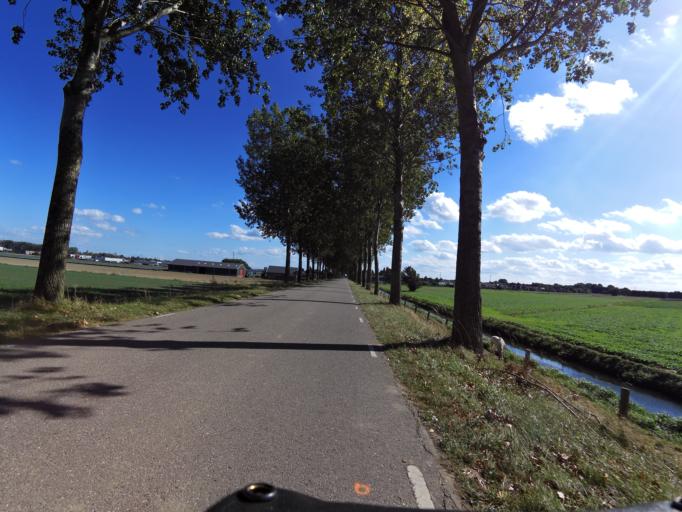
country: NL
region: South Holland
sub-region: Gemeente Zwijndrecht
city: Zwijndrecht
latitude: 51.7905
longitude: 4.6017
